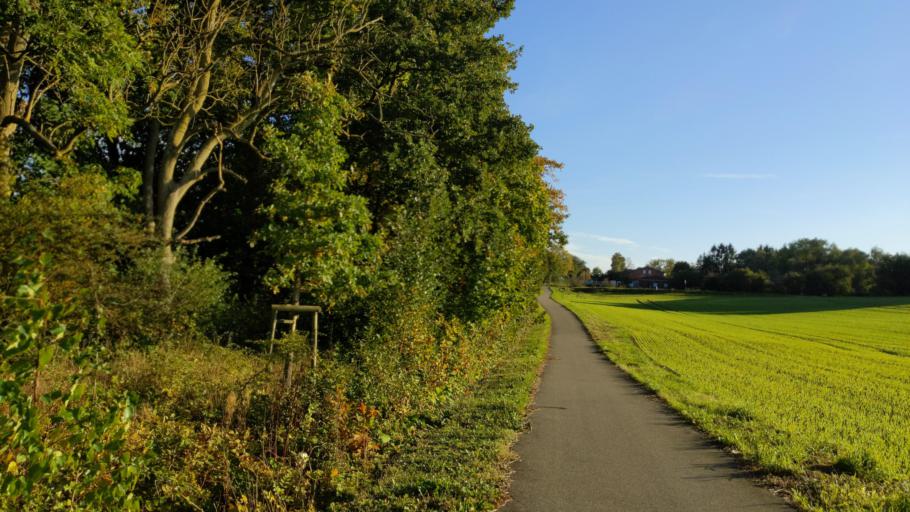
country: DE
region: Schleswig-Holstein
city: Ahrensbok
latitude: 54.0280
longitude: 10.5641
